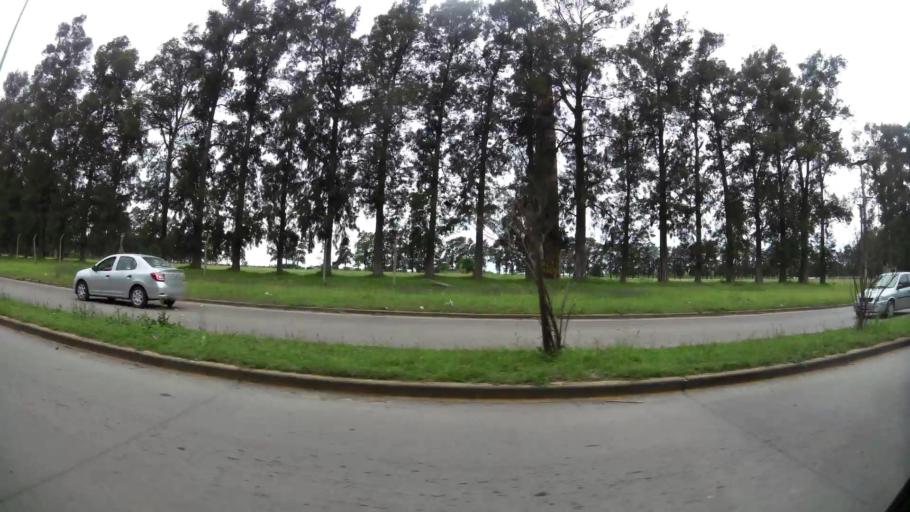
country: AR
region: Buenos Aires
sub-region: Partido de Campana
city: Campana
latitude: -34.1776
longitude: -58.9424
